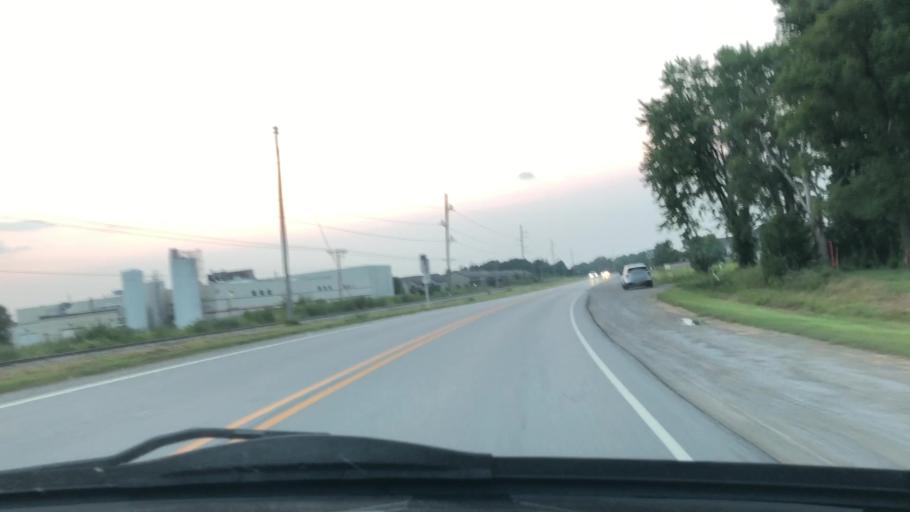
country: US
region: Iowa
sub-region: Johnson County
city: North Liberty
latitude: 41.7621
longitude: -91.6117
